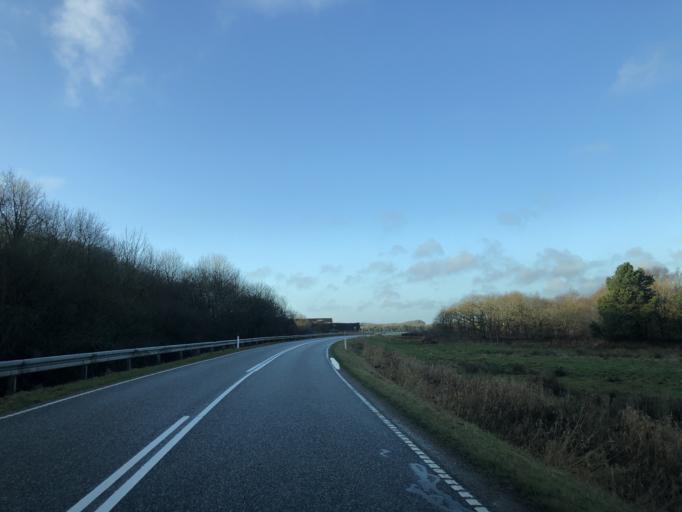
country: DK
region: Central Jutland
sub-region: Struer Kommune
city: Struer
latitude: 56.5412
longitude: 8.5071
